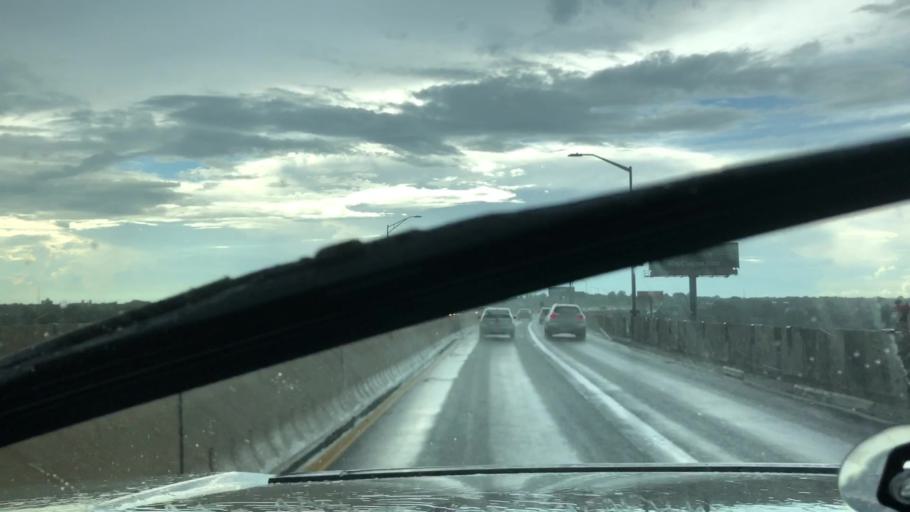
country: US
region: New Jersey
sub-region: Middlesex County
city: Perth Amboy
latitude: 40.5243
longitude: -74.2553
